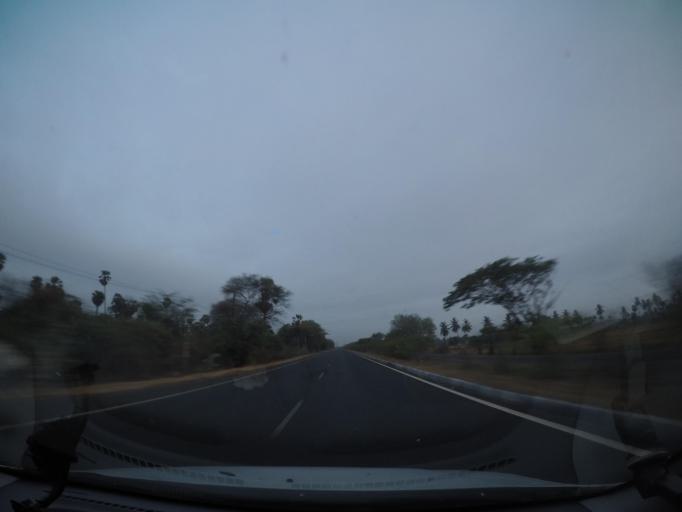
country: IN
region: Andhra Pradesh
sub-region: West Godavari
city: Tadepallegudem
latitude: 16.8102
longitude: 81.3432
